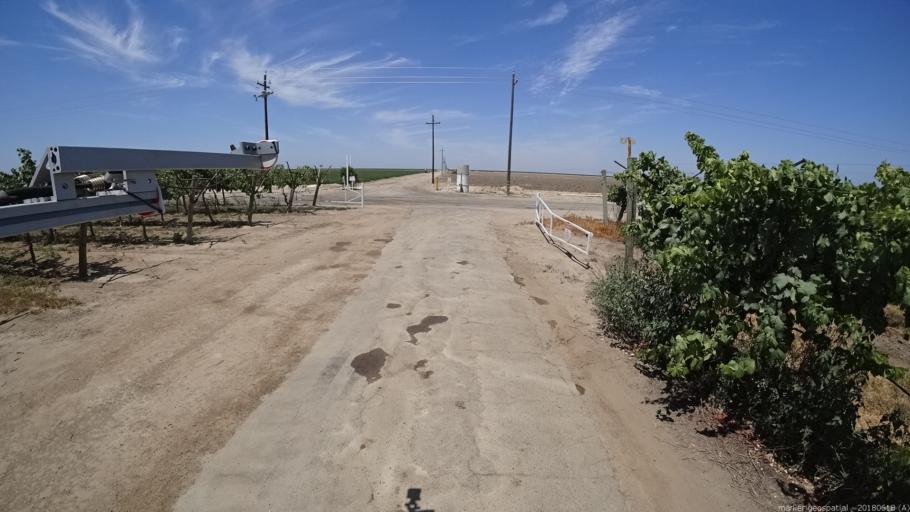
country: US
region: California
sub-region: Madera County
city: Parkwood
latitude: 36.8875
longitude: -120.1648
